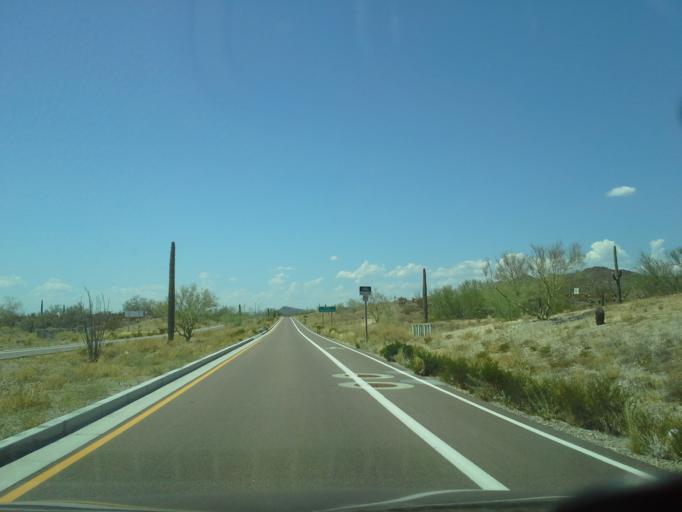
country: US
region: Arizona
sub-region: Maricopa County
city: Anthem
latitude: 33.7818
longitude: -112.0819
